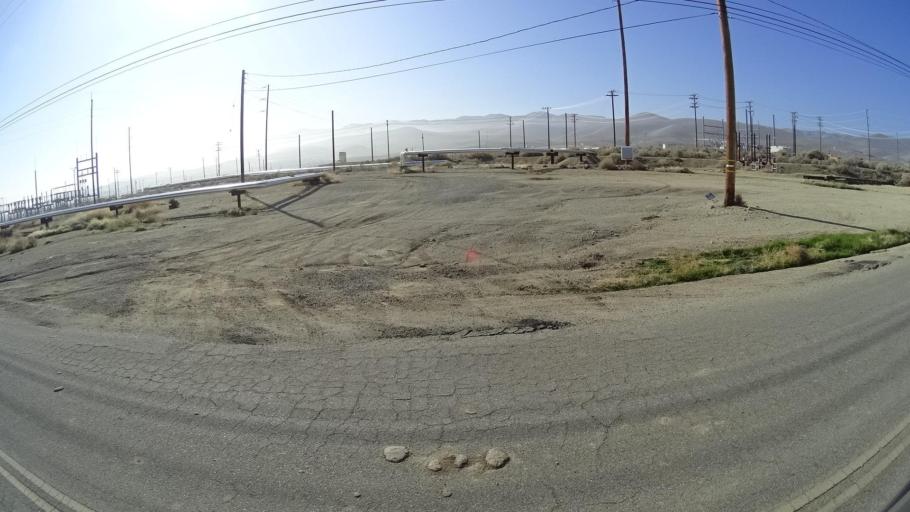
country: US
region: California
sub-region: Kern County
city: Taft Heights
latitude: 35.2265
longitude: -119.6285
